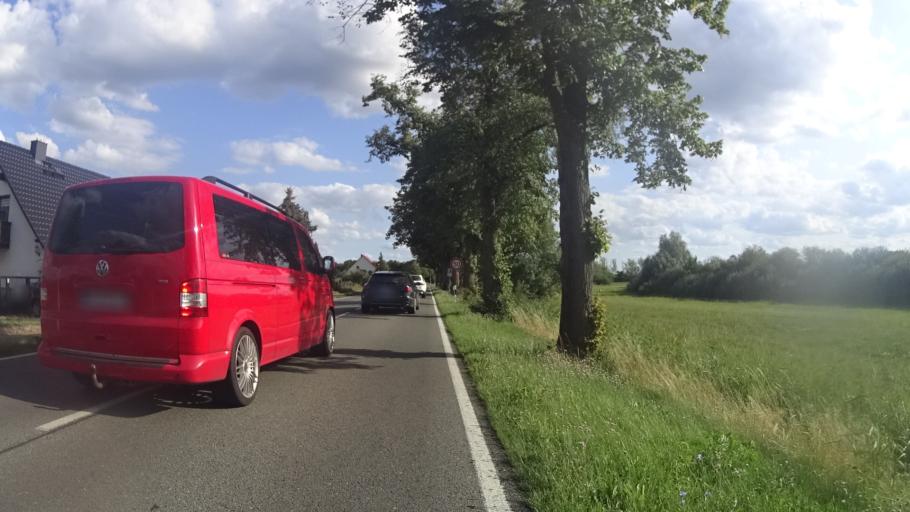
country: DE
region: Brandenburg
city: Rathenow
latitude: 52.6333
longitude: 12.3313
